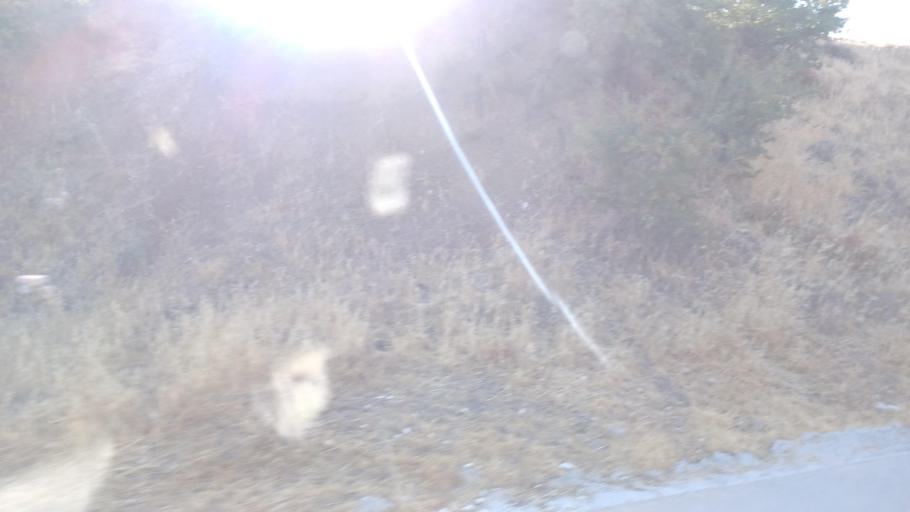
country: CY
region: Pafos
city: Mesogi
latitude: 34.8716
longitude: 32.6092
